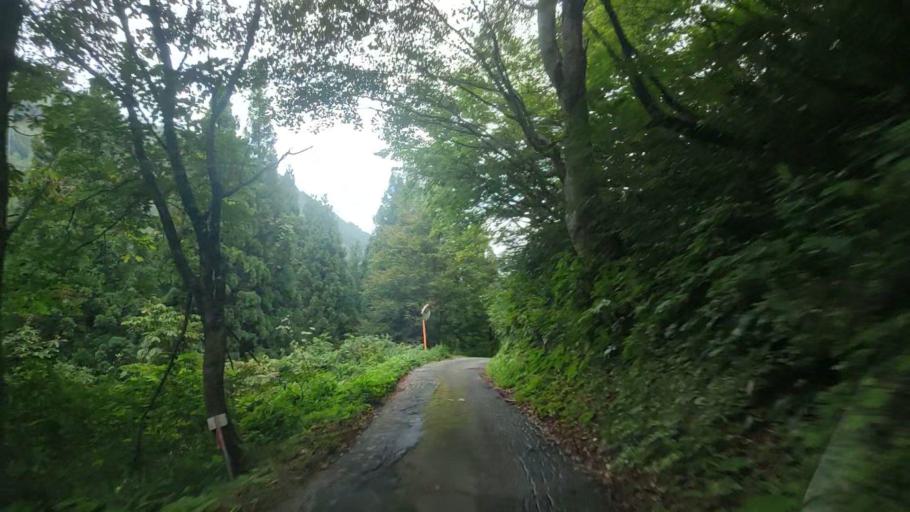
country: JP
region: Toyama
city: Yatsuomachi-higashikumisaka
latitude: 36.4046
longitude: 137.0756
